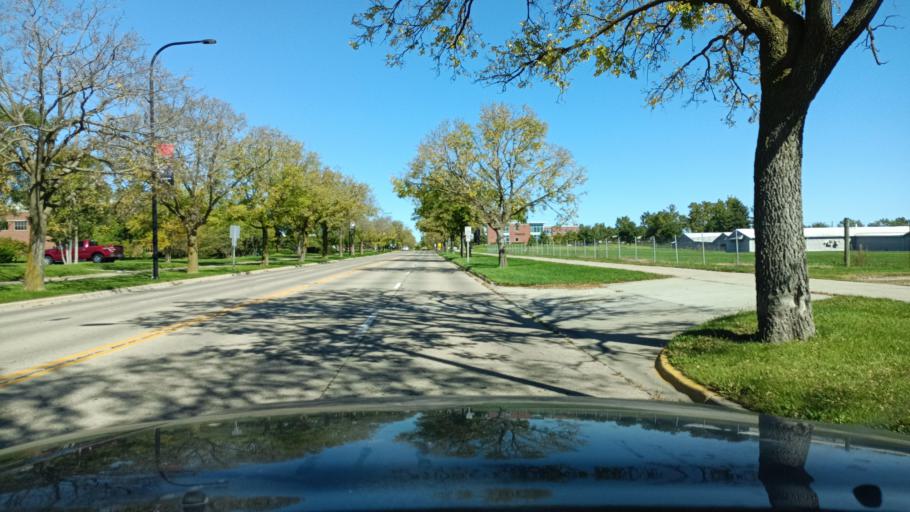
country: US
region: Illinois
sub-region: Champaign County
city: Champaign
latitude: 40.0886
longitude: -88.2382
